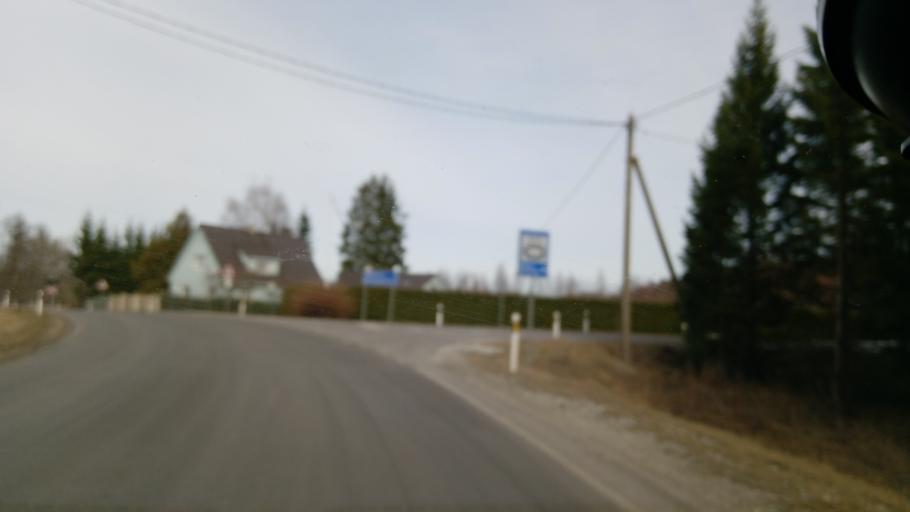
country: EE
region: Raplamaa
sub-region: Rapla vald
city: Rapla
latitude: 59.0180
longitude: 24.8381
